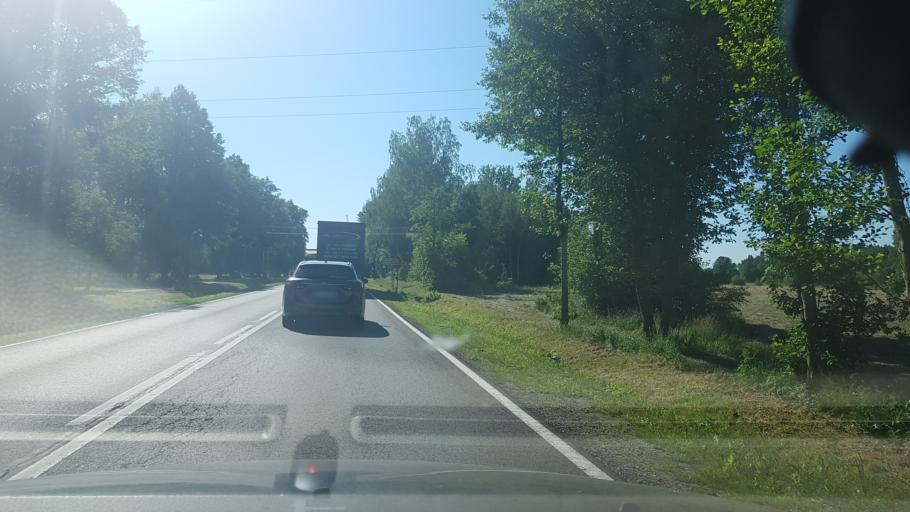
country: PL
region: Masovian Voivodeship
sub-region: Powiat wegrowski
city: Lochow
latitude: 52.5413
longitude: 21.6490
